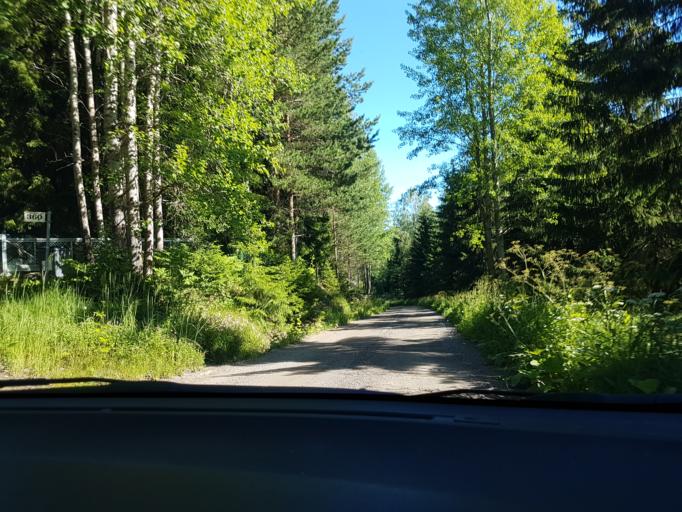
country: FI
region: Uusimaa
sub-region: Helsinki
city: Sibbo
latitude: 60.2908
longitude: 25.2408
